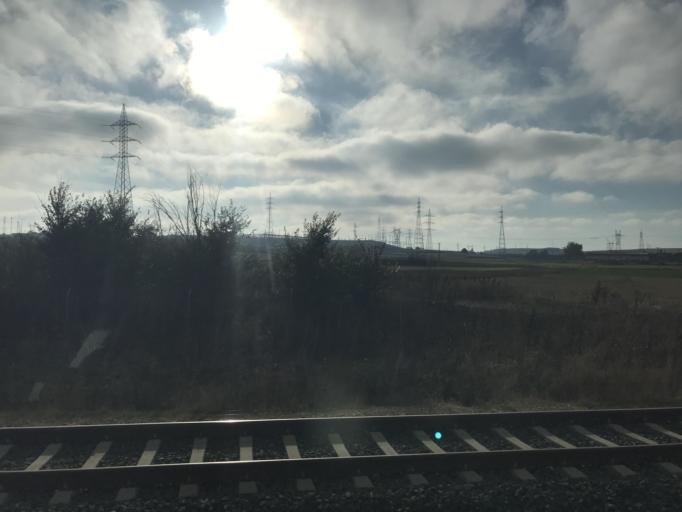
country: ES
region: Castille and Leon
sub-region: Provincia de Burgos
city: Villalbilla de Burgos
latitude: 42.3454
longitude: -3.7887
